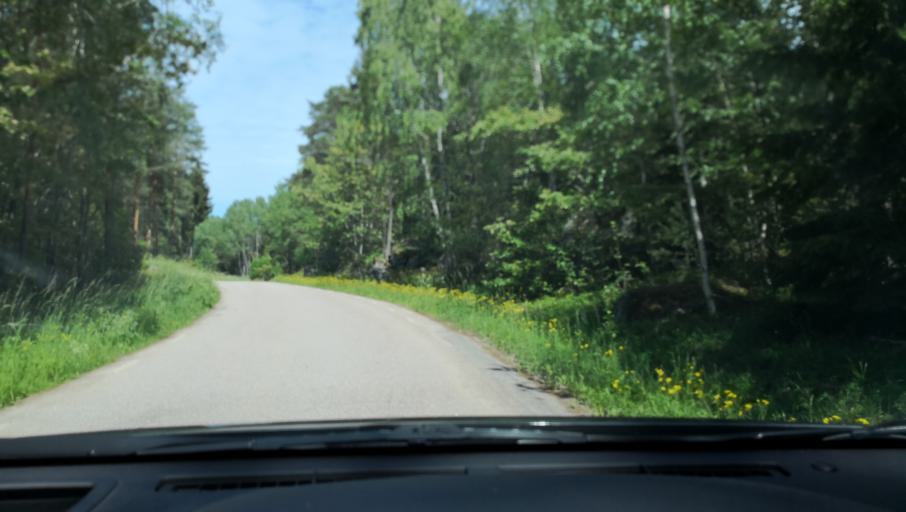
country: SE
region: Stockholm
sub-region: Sigtuna Kommun
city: Sigtuna
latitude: 59.6996
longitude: 17.6482
